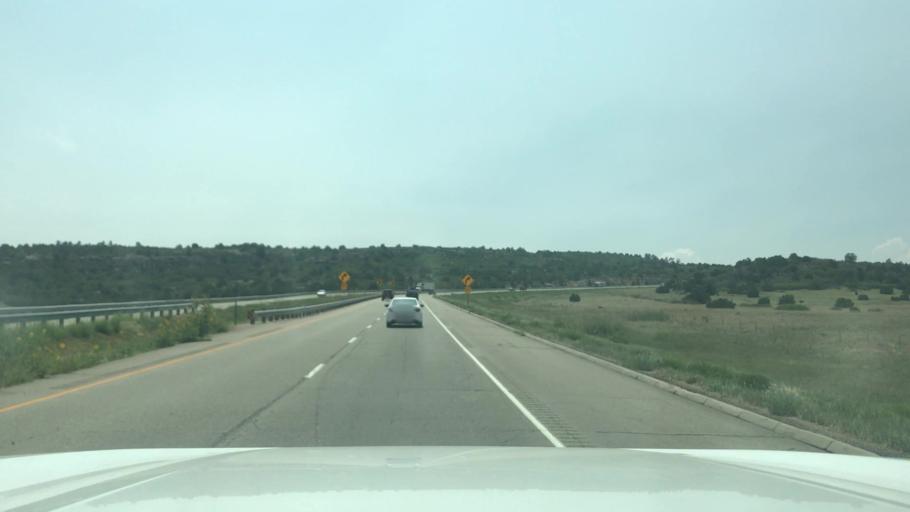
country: US
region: Colorado
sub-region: Pueblo County
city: Colorado City
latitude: 37.9439
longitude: -104.8051
